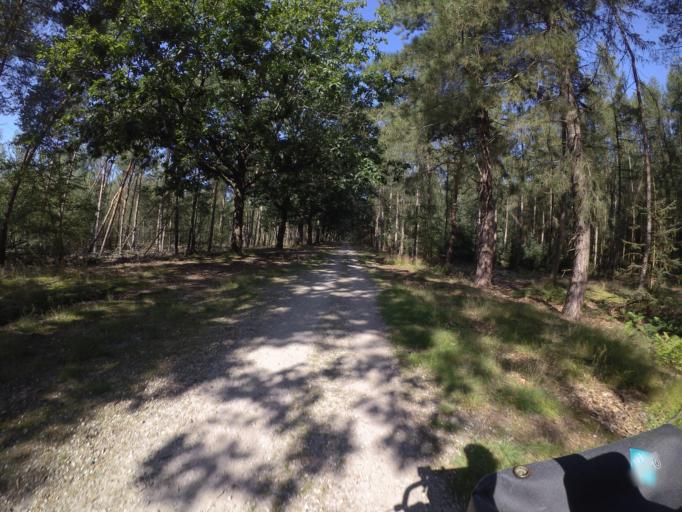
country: NL
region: North Brabant
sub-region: Gemeente Mill en Sint Hubert
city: Wilbertoord
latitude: 51.6619
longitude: 5.7895
